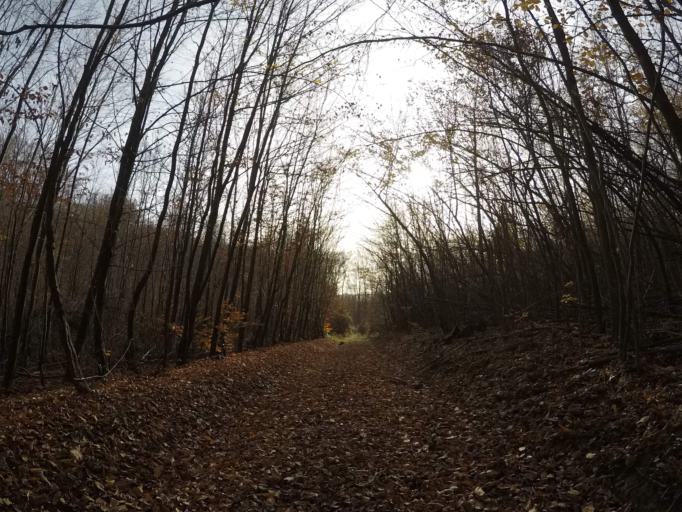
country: SK
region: Presovsky
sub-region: Okres Presov
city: Presov
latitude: 48.9165
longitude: 21.2123
